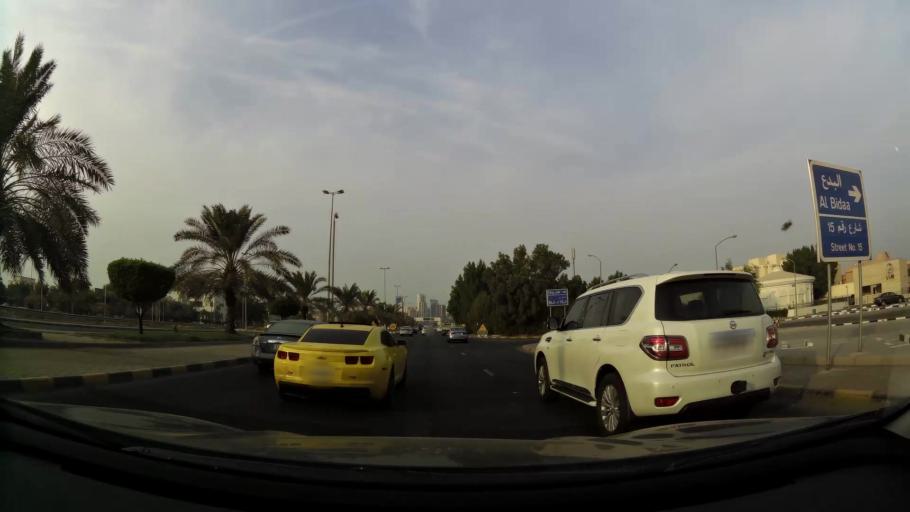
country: KW
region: Muhafazat Hawalli
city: Ar Rumaythiyah
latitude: 29.3143
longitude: 48.0871
